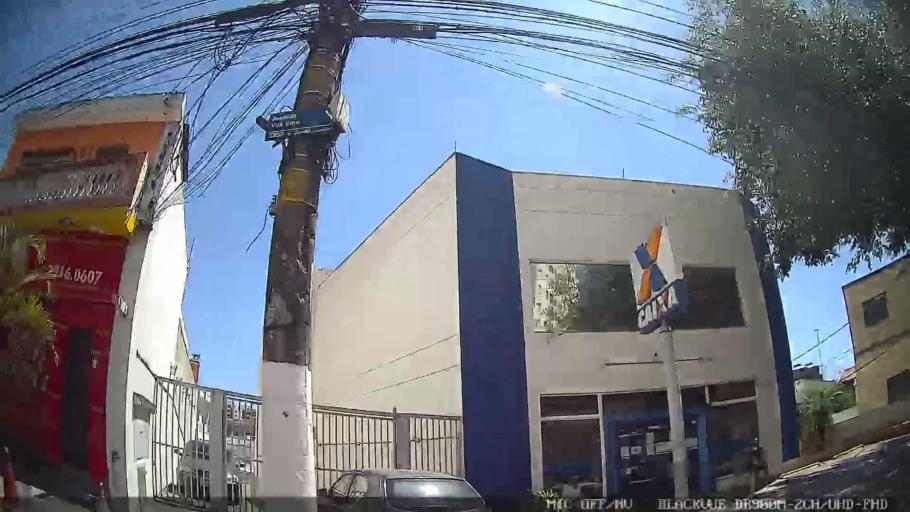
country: BR
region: Sao Paulo
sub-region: Sao Caetano Do Sul
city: Sao Caetano do Sul
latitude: -23.5892
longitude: -46.5429
